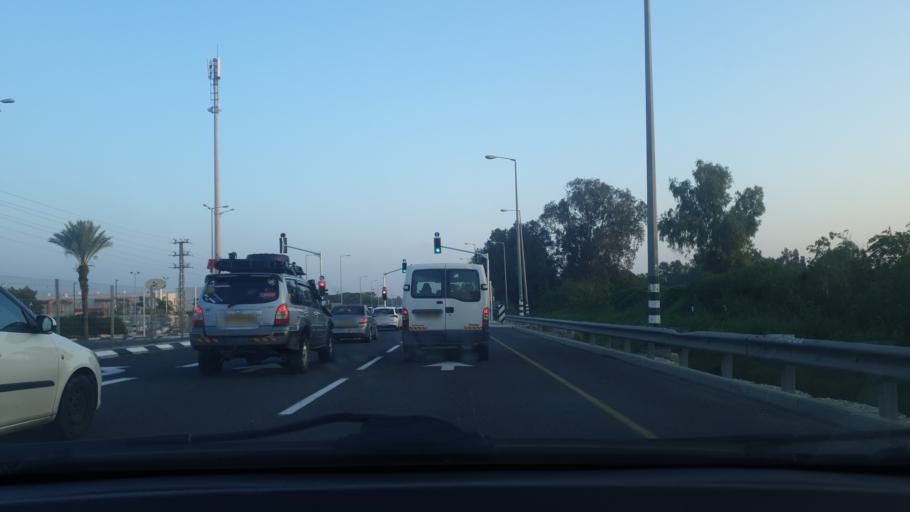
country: IL
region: Central District
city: Kefar Habad
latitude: 31.9642
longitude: 34.8481
